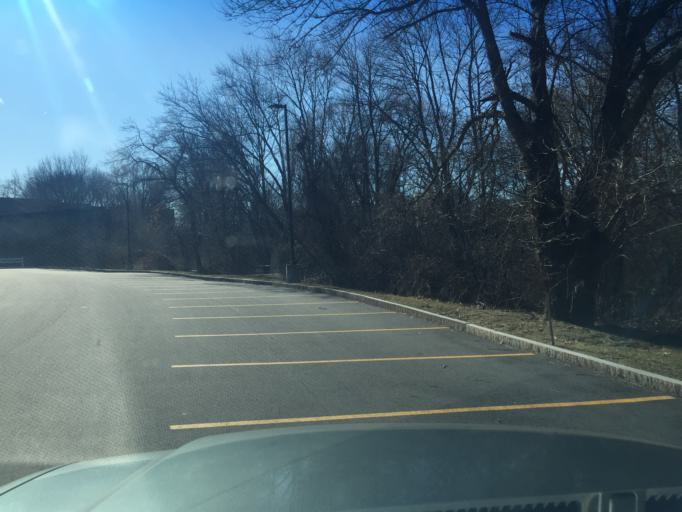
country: US
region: Massachusetts
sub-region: Norfolk County
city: Norwood
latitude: 42.1766
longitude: -71.1929
